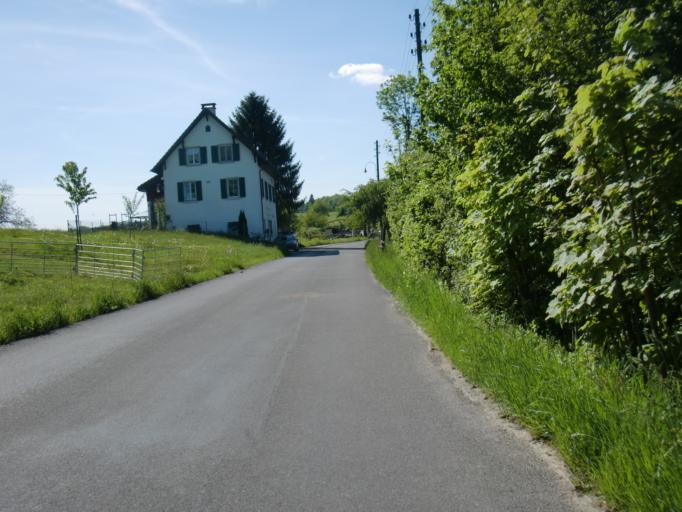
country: CH
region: Zurich
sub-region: Bezirk Meilen
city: Hombrechtikon
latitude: 47.2679
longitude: 8.7773
